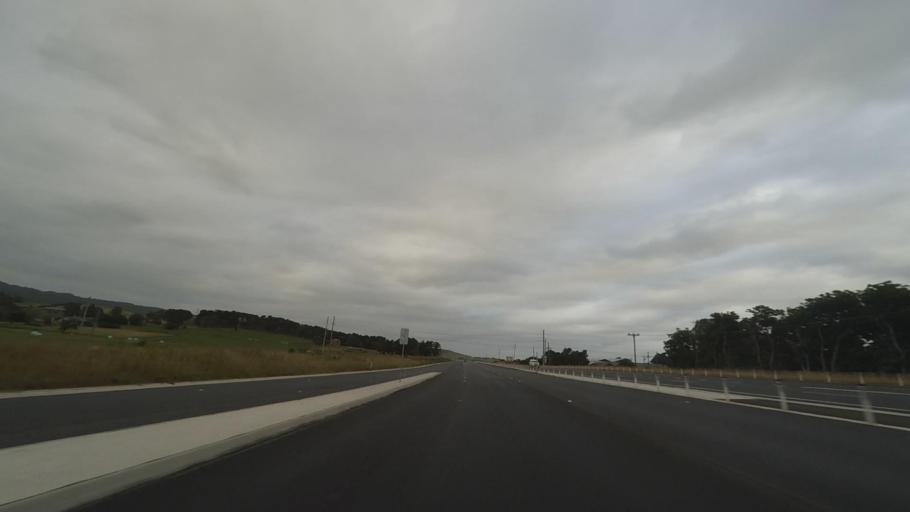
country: AU
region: New South Wales
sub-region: Kiama
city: Gerringong
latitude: -34.7445
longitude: 150.8160
